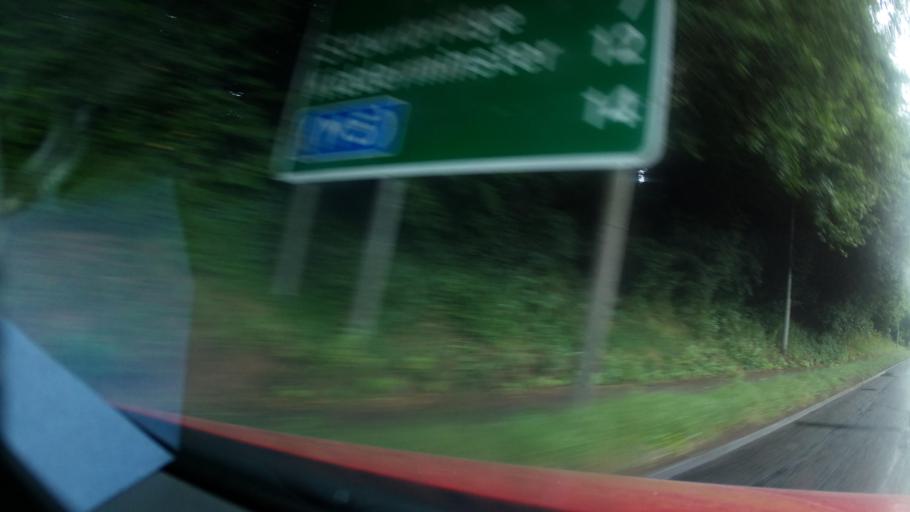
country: GB
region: England
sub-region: Dudley
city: Kingswinford
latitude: 52.5531
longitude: -2.1727
